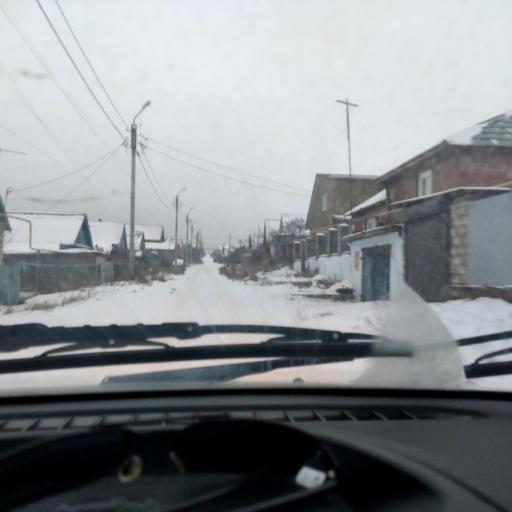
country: RU
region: Samara
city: Zhigulevsk
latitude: 53.4895
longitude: 49.5303
